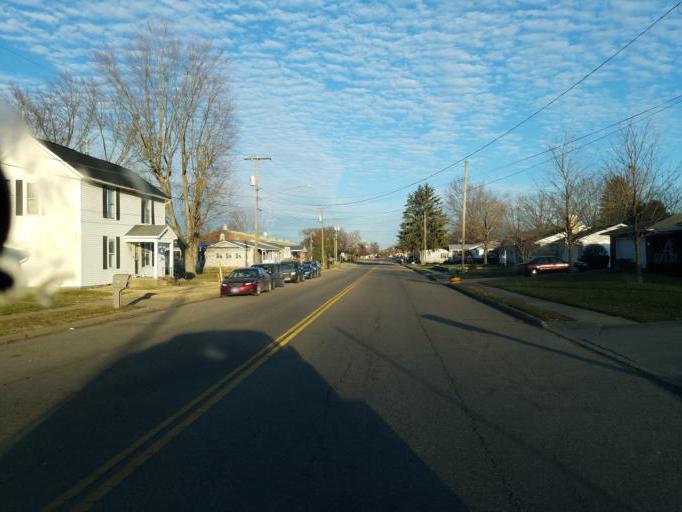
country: US
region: Ohio
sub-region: Muskingum County
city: Dresden
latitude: 40.1192
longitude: -82.0143
